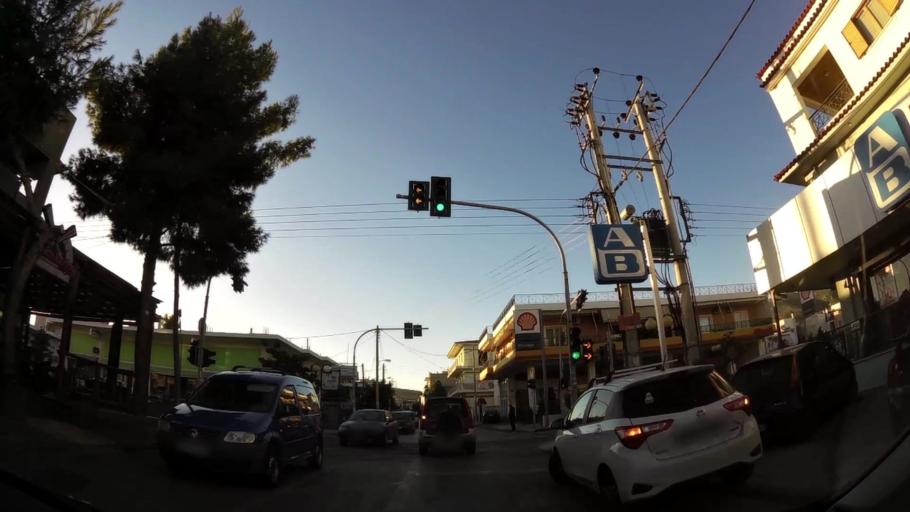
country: GR
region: Attica
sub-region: Nomarchia Dytikis Attikis
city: Ano Liosia
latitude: 38.0864
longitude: 23.7083
